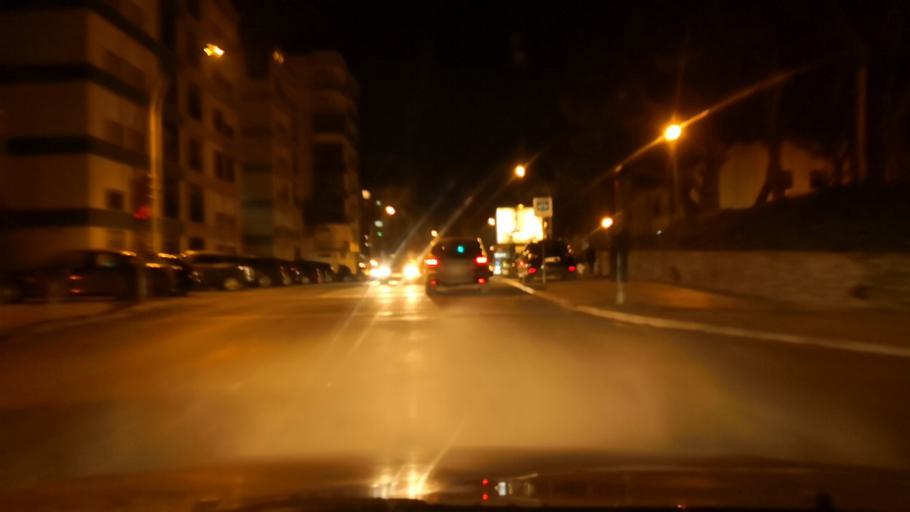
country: PT
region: Setubal
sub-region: Setubal
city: Setubal
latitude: 38.5400
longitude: -8.8952
